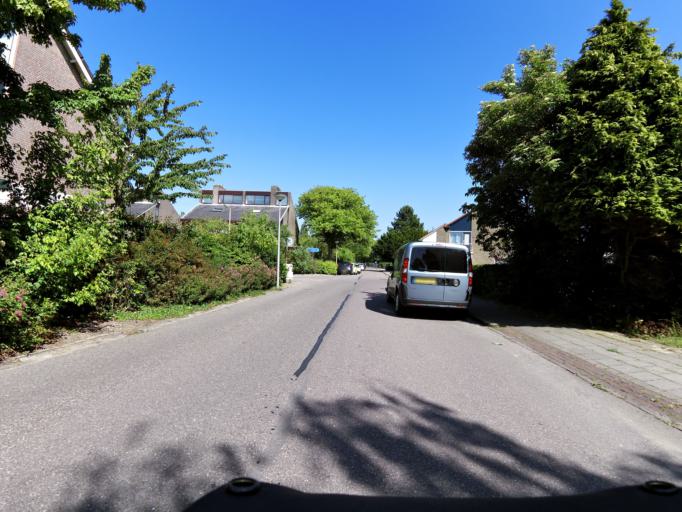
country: NL
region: South Holland
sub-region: Gemeente Brielle
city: Brielle
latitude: 51.9110
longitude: 4.1668
